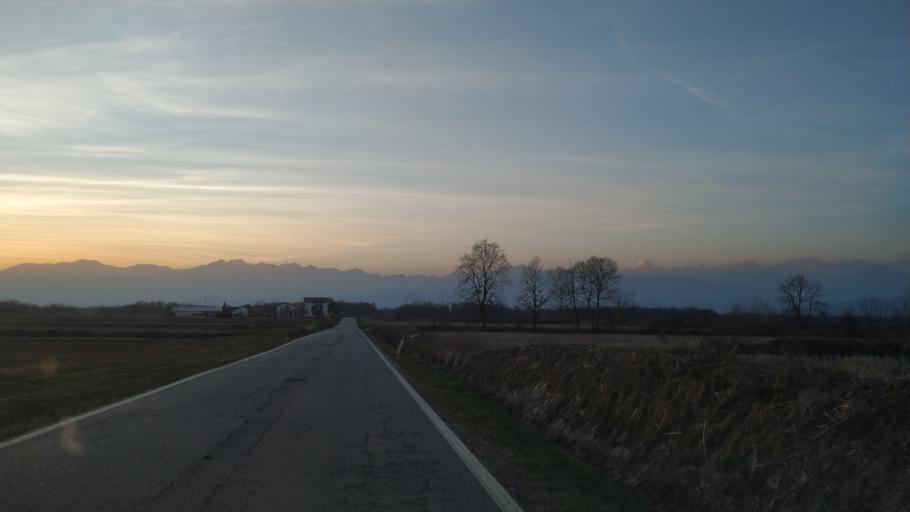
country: IT
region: Piedmont
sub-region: Provincia di Vercelli
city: Rovasenda
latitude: 45.5438
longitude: 8.2854
